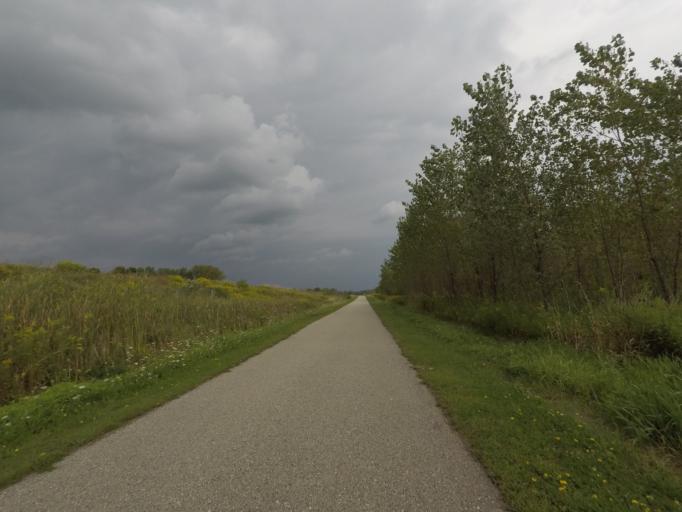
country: US
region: Wisconsin
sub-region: Jefferson County
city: Fort Atkinson
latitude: 42.9576
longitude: -88.8281
